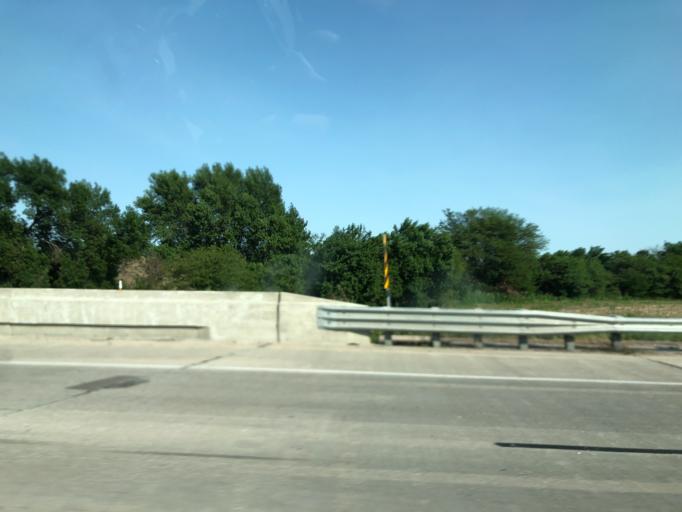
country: US
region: Nebraska
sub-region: Saunders County
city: Ashland
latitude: 40.9473
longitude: -96.4216
